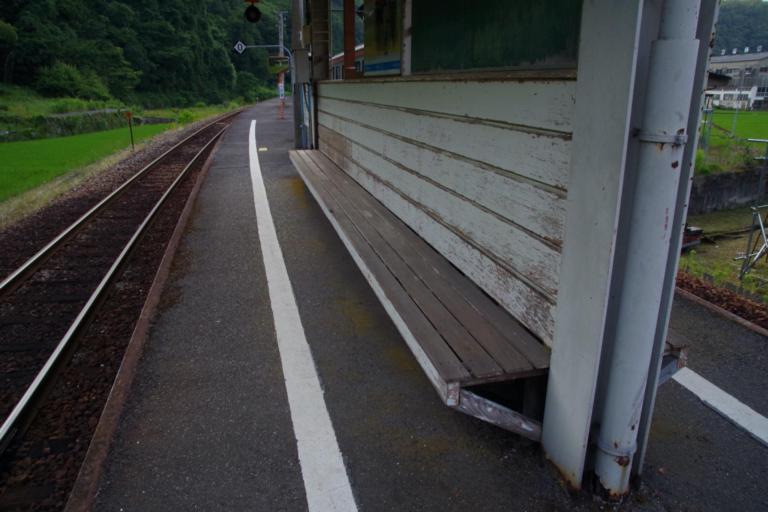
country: JP
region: Hiroshima
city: Miyoshi
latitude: 34.8846
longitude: 132.6712
